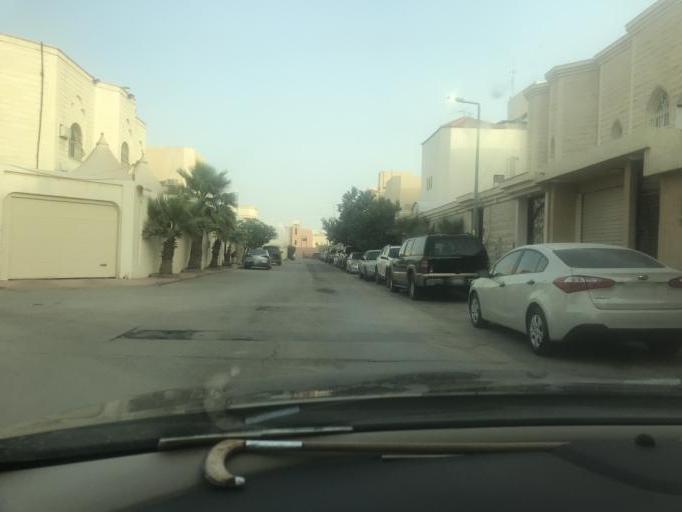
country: SA
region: Ar Riyad
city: Riyadh
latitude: 24.7455
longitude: 46.7792
